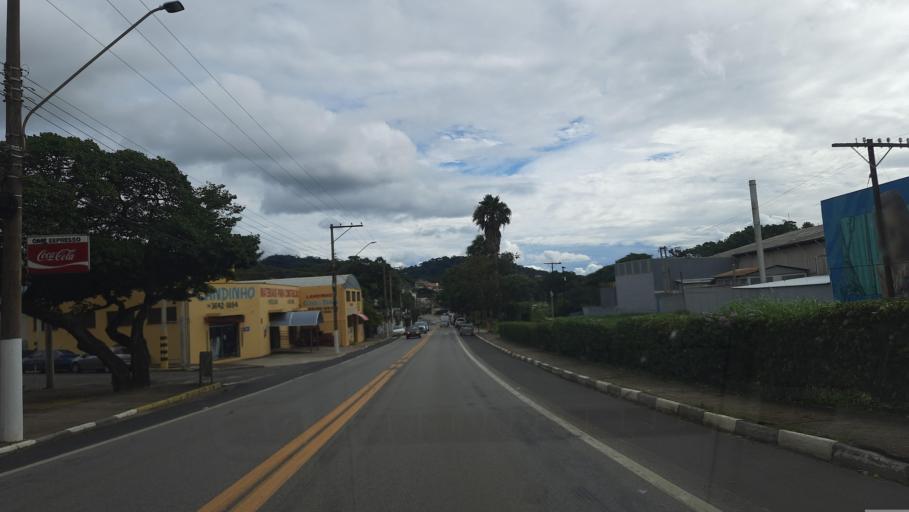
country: BR
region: Sao Paulo
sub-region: Sao Joao Da Boa Vista
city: Sao Joao da Boa Vista
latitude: -21.9403
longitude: -46.7153
